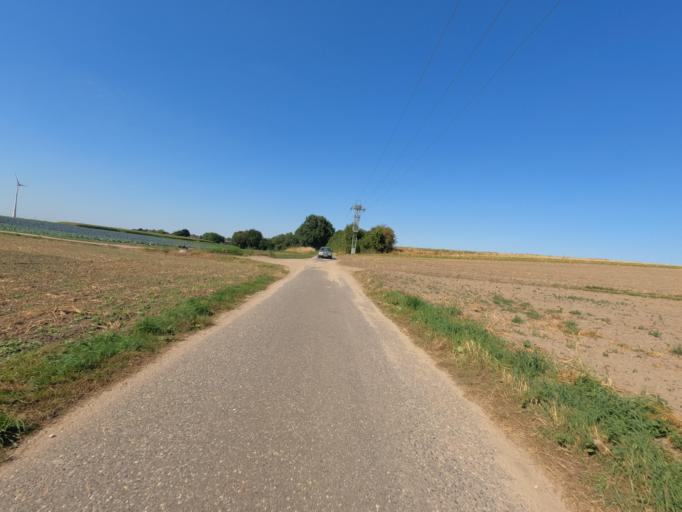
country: DE
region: North Rhine-Westphalia
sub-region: Regierungsbezirk Dusseldorf
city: Niederkruchten
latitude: 51.1847
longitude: 6.1976
